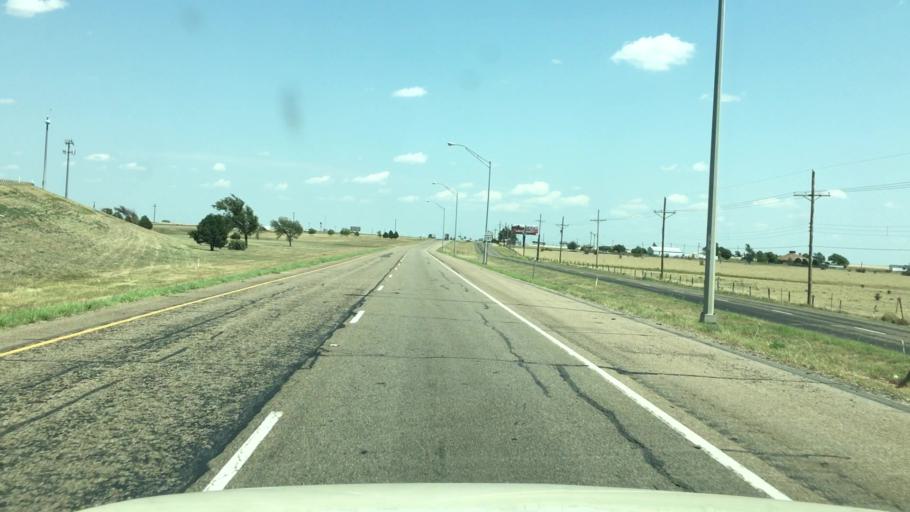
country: US
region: Texas
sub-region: Potter County
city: Amarillo
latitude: 35.1926
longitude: -101.6953
